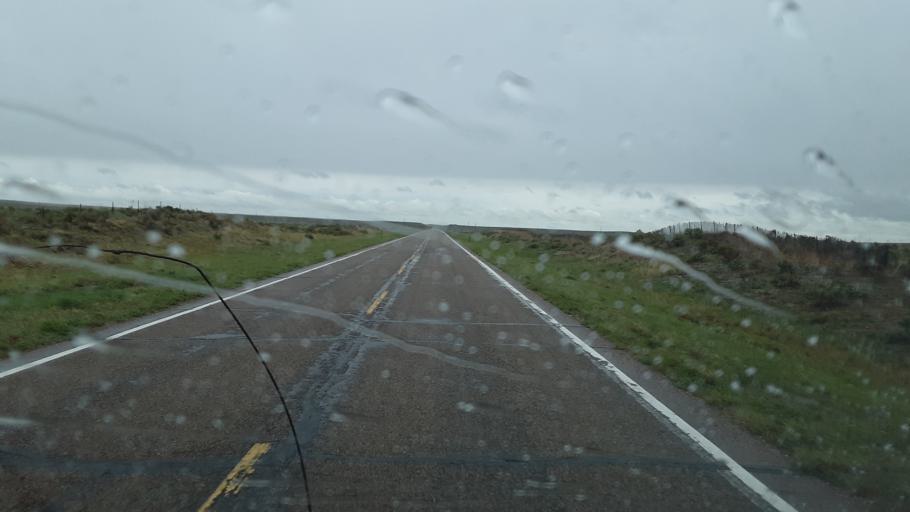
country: US
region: Colorado
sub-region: Lincoln County
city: Hugo
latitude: 38.8497
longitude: -103.1906
